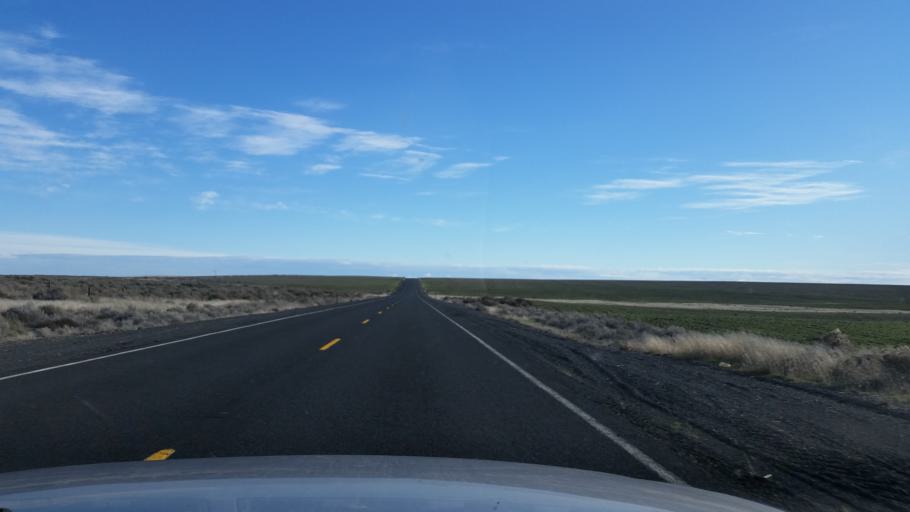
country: US
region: Washington
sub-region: Grant County
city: Moses Lake
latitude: 47.3561
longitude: -118.9514
